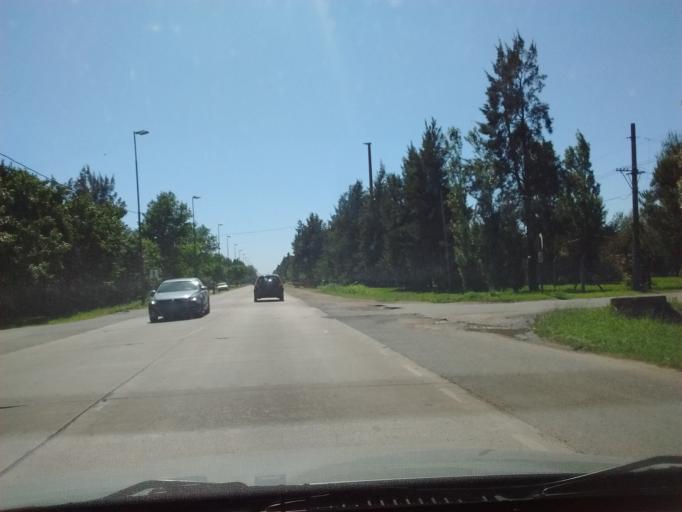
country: AR
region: Santa Fe
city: Funes
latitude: -32.9094
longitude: -60.7689
